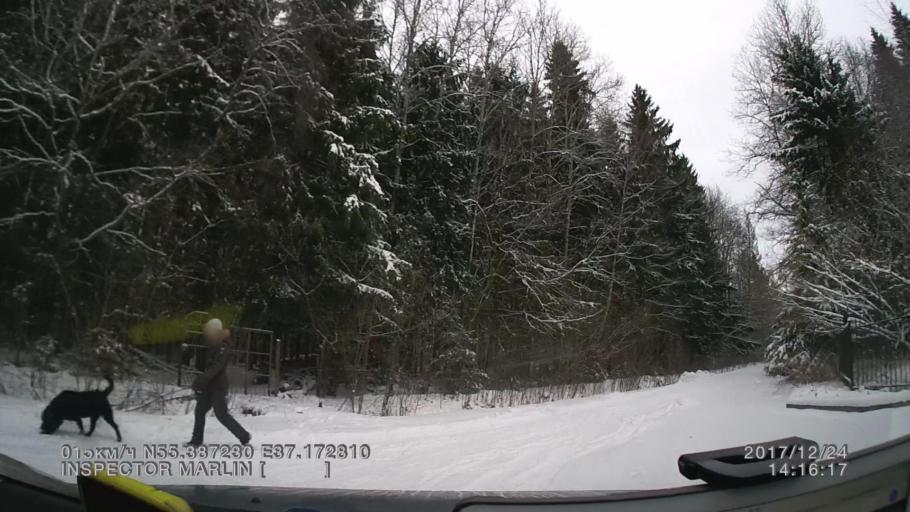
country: RU
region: Moskovskaya
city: Troitsk
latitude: 55.3873
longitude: 37.1728
